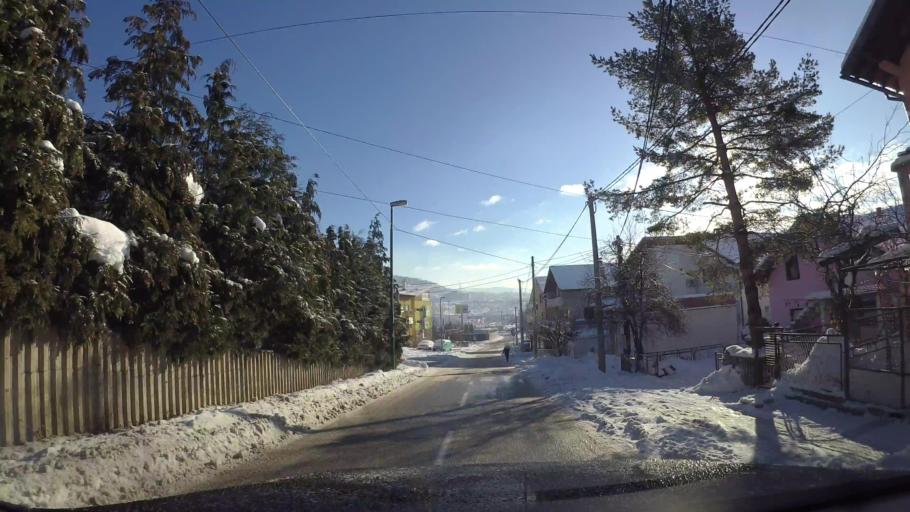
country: BA
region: Federation of Bosnia and Herzegovina
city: Kobilja Glava
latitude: 43.8803
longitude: 18.3960
